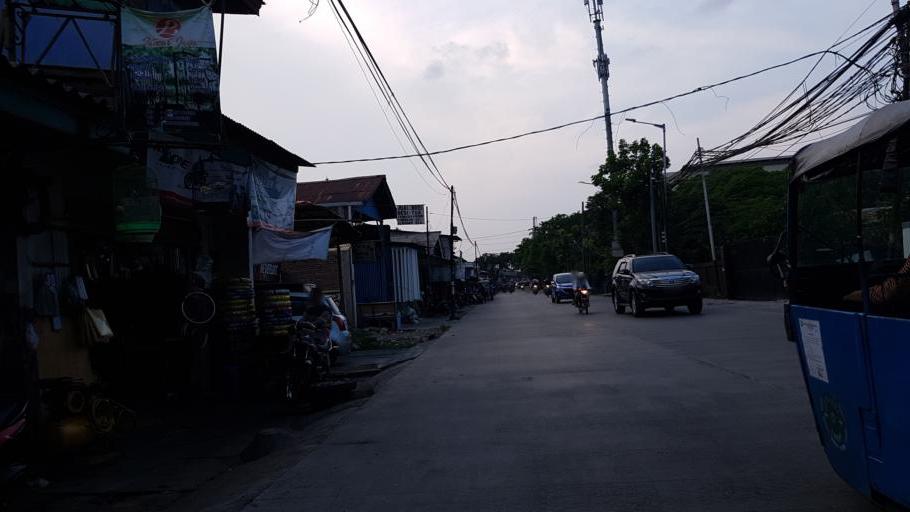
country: ID
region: West Java
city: Teluknaga
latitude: -6.1280
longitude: 106.7405
